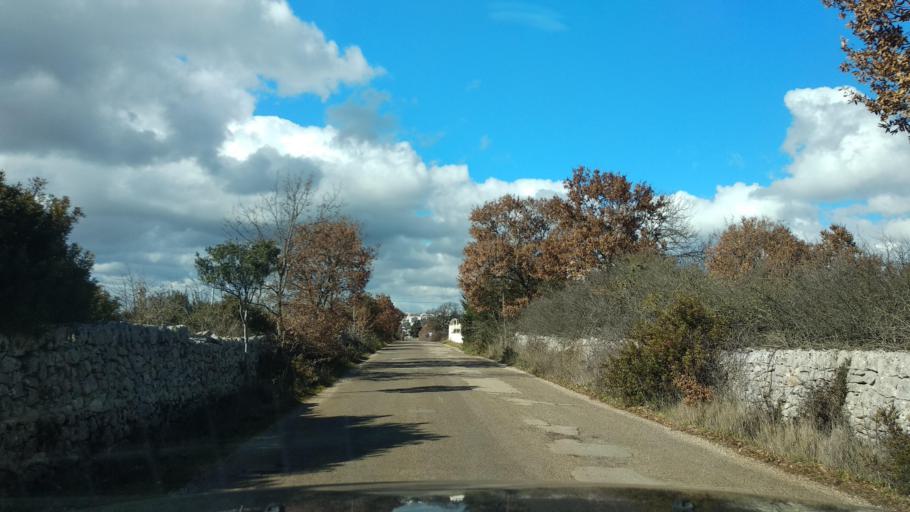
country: IT
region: Apulia
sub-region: Provincia di Brindisi
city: Casalini
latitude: 40.7211
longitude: 17.4475
